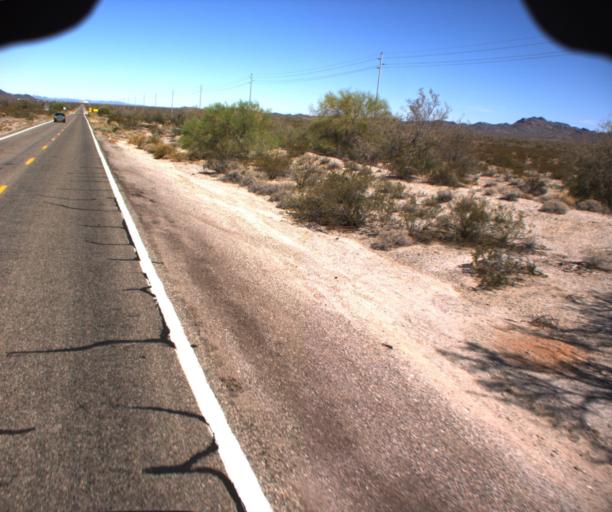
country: US
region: Arizona
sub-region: La Paz County
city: Salome
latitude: 33.7262
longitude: -113.7088
